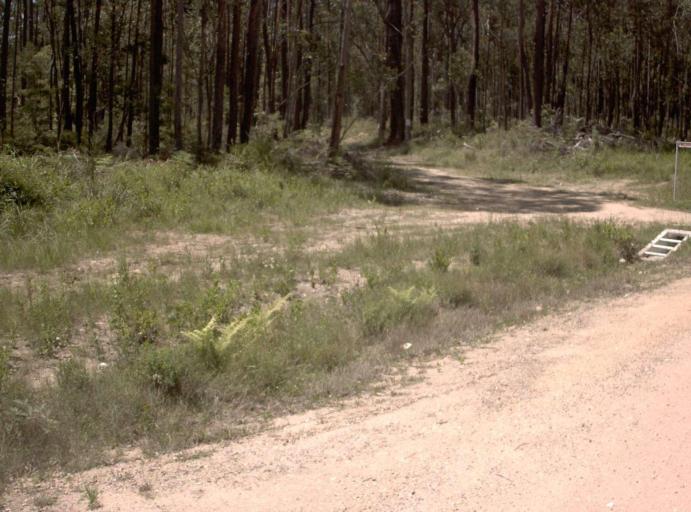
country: AU
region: Victoria
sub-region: East Gippsland
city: Lakes Entrance
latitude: -37.6771
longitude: 148.7846
